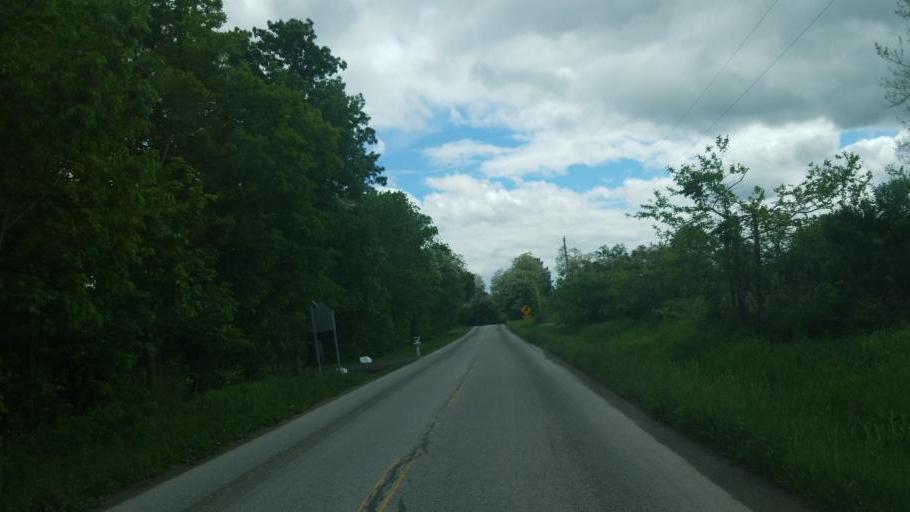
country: US
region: Ohio
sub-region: Geauga County
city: Middlefield
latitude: 41.4248
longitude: -81.0034
